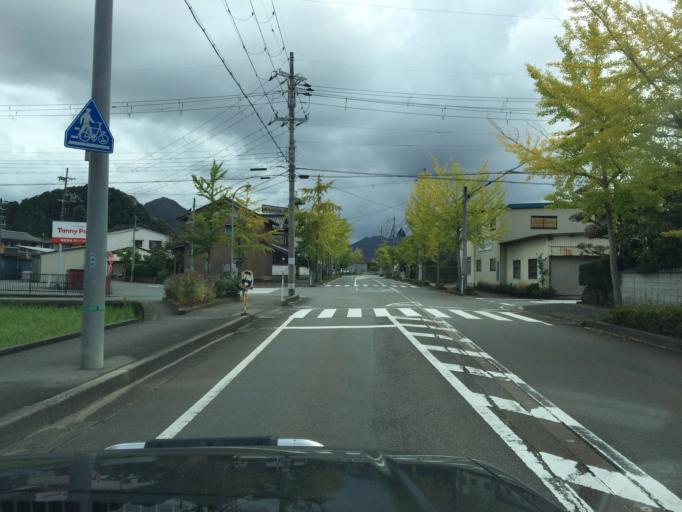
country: JP
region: Hyogo
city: Toyooka
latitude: 35.4727
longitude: 134.7764
